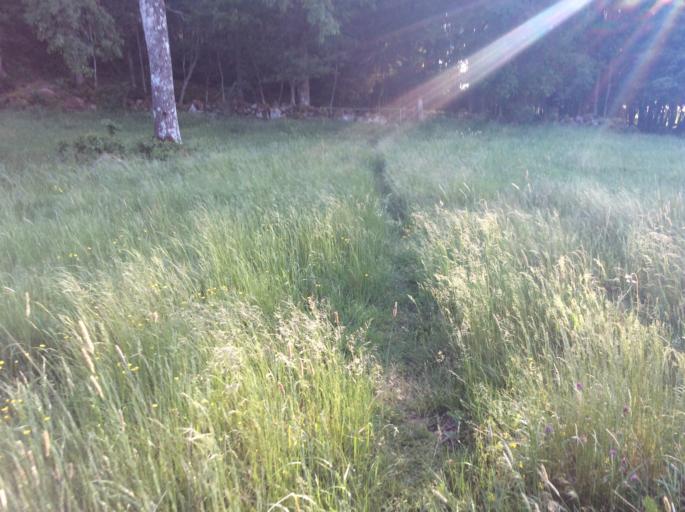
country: SE
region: Vaestra Goetaland
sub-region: Goteborg
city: Torslanda
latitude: 57.7965
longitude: 11.8561
